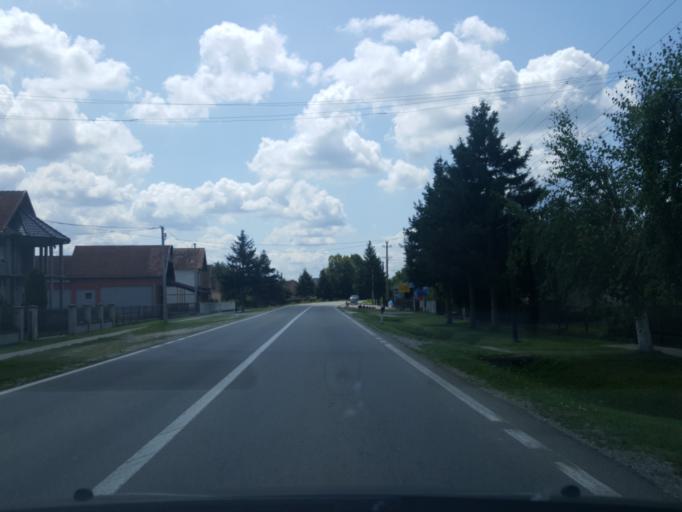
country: RS
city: Ribari
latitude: 44.7211
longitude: 19.4465
